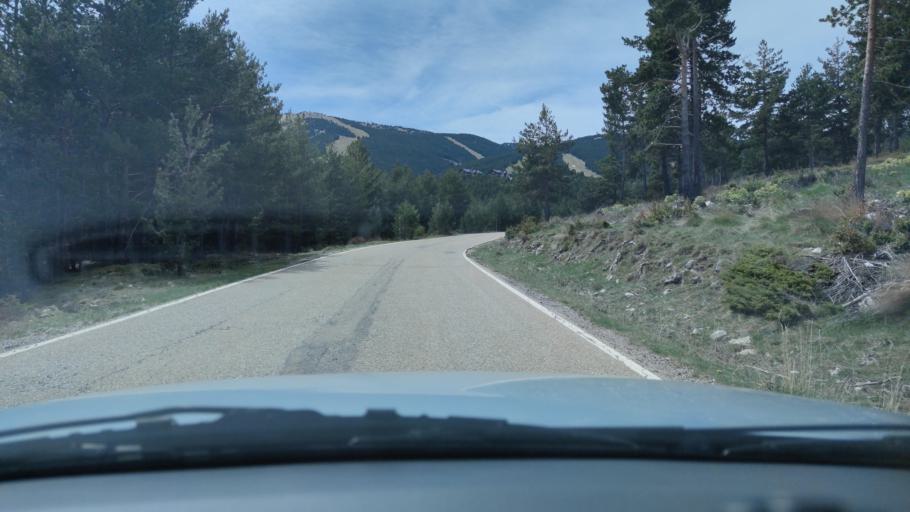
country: ES
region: Catalonia
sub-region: Provincia de Lleida
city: Gosol
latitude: 42.1825
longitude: 1.5588
